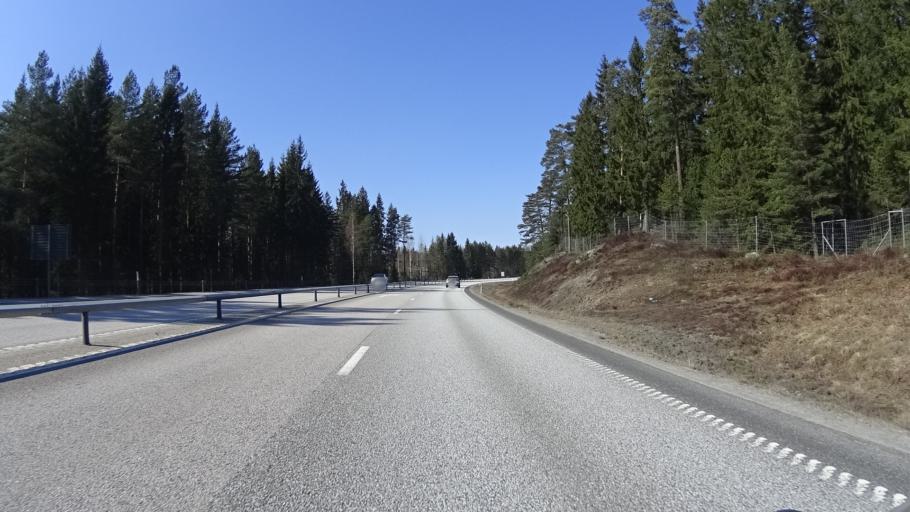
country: SE
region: OErebro
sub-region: Karlskoga Kommun
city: Karlskoga
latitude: 59.2984
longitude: 14.6430
